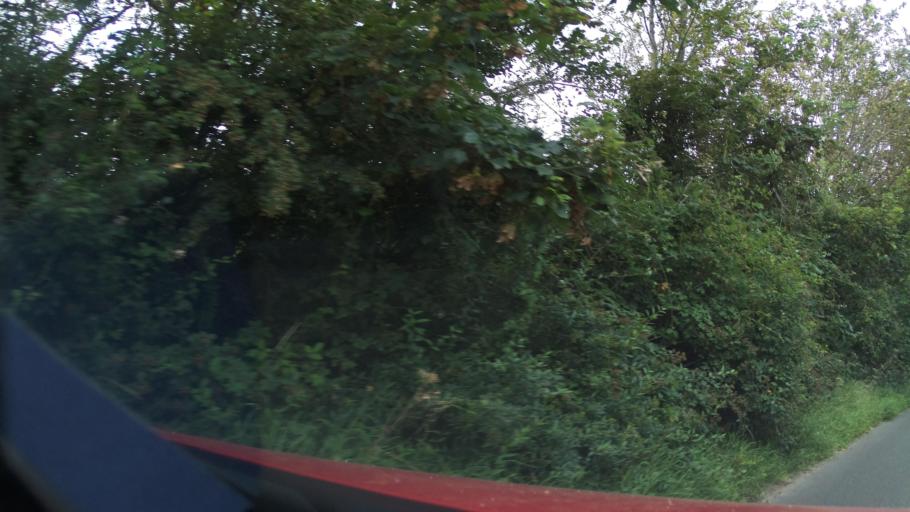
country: GB
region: England
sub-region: Hampshire
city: Milford on Sea
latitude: 50.7337
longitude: -1.5898
